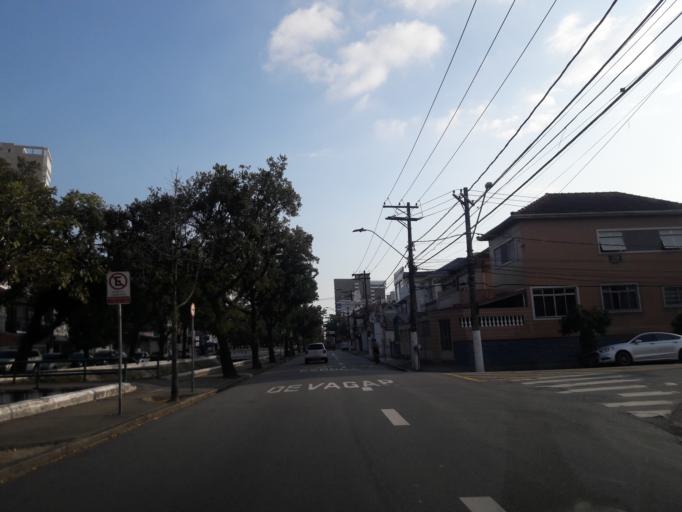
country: BR
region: Sao Paulo
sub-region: Santos
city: Santos
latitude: -23.9509
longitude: -46.3372
